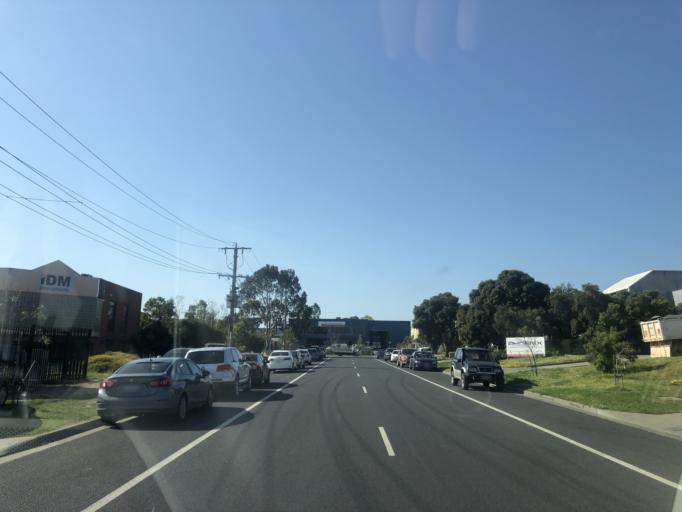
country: AU
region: Victoria
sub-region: Casey
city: Hallam
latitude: -38.0148
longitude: 145.2746
